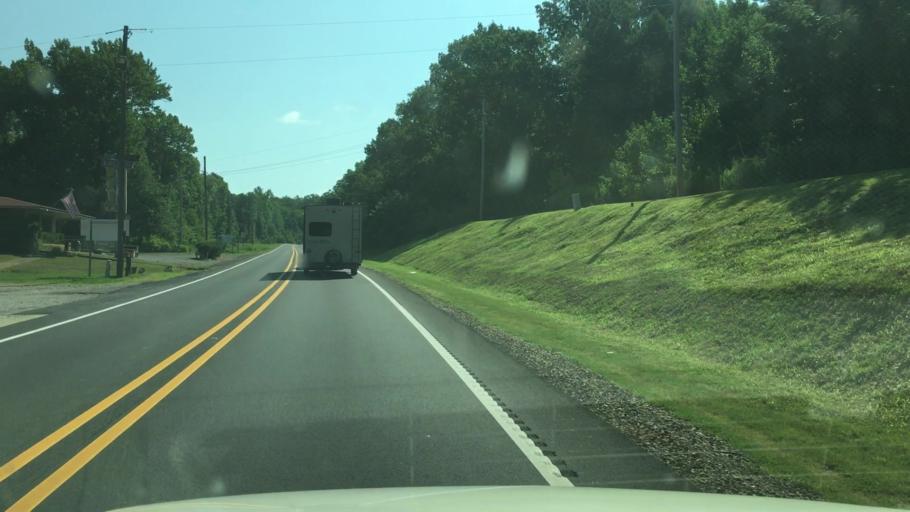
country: US
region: Arkansas
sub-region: Garland County
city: Rockwell
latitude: 34.5219
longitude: -93.3359
